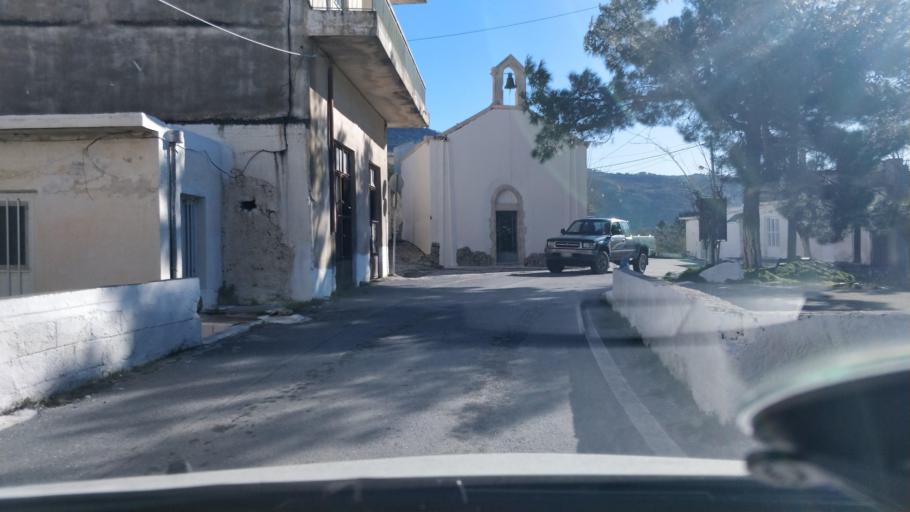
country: GR
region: Crete
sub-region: Nomos Lasithiou
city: Kritsa
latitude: 35.0793
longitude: 25.5847
